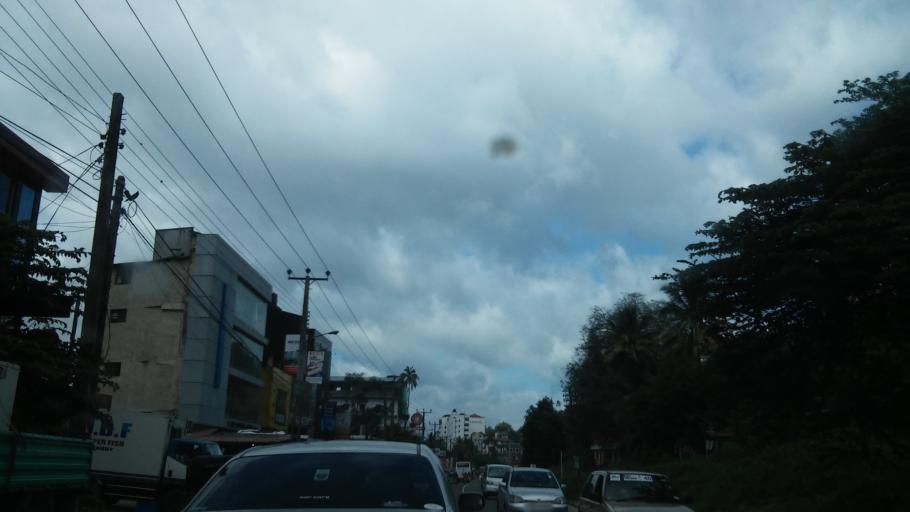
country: LK
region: Central
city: Kandy
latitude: 7.2800
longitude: 80.6208
